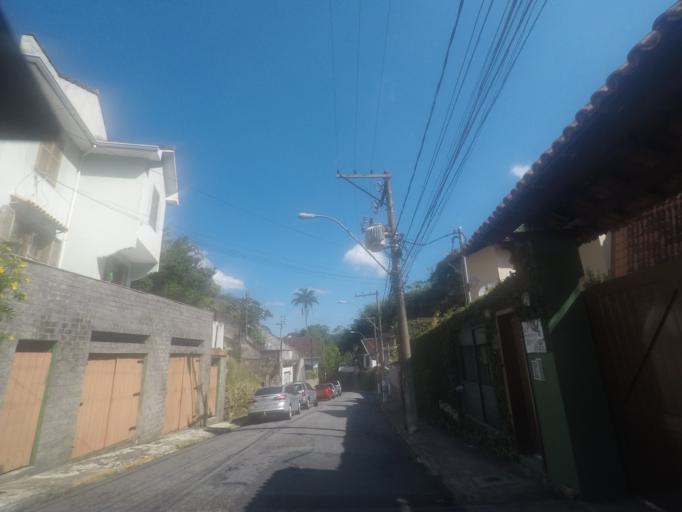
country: BR
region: Rio de Janeiro
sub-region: Petropolis
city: Petropolis
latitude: -22.5188
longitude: -43.1890
